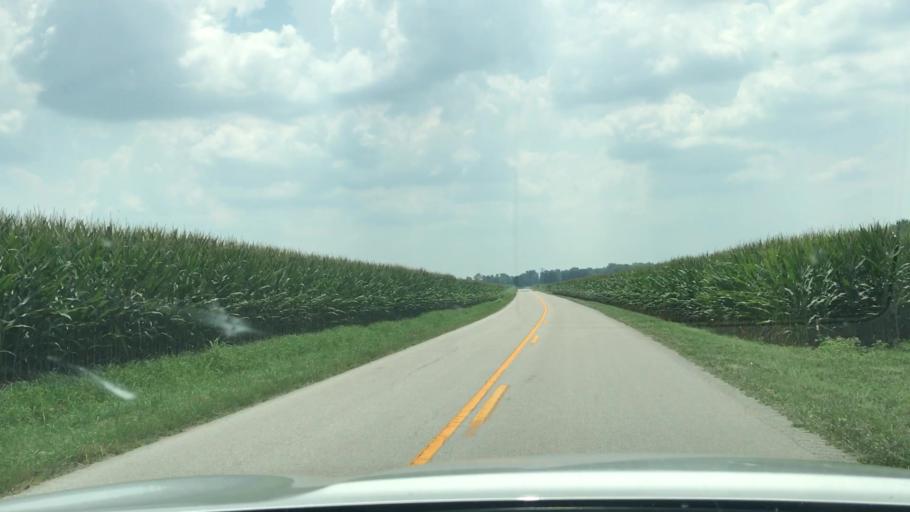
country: US
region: Kentucky
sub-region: Todd County
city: Elkton
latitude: 36.7522
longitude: -87.0966
